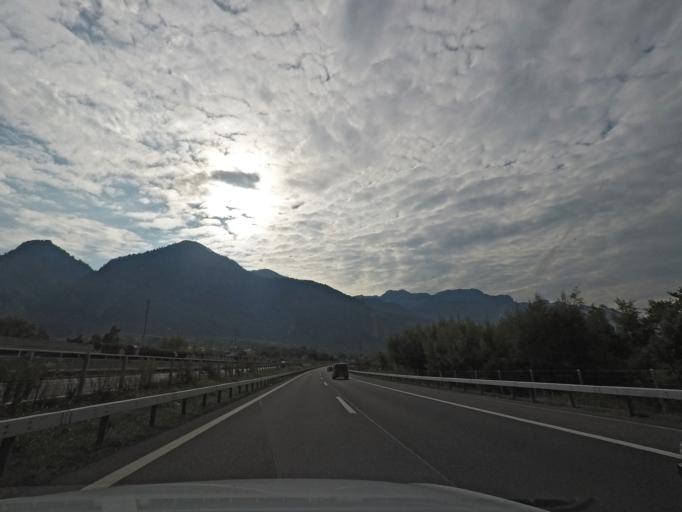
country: CH
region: Grisons
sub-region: Landquart District
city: Zizers
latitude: 46.9341
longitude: 9.5565
